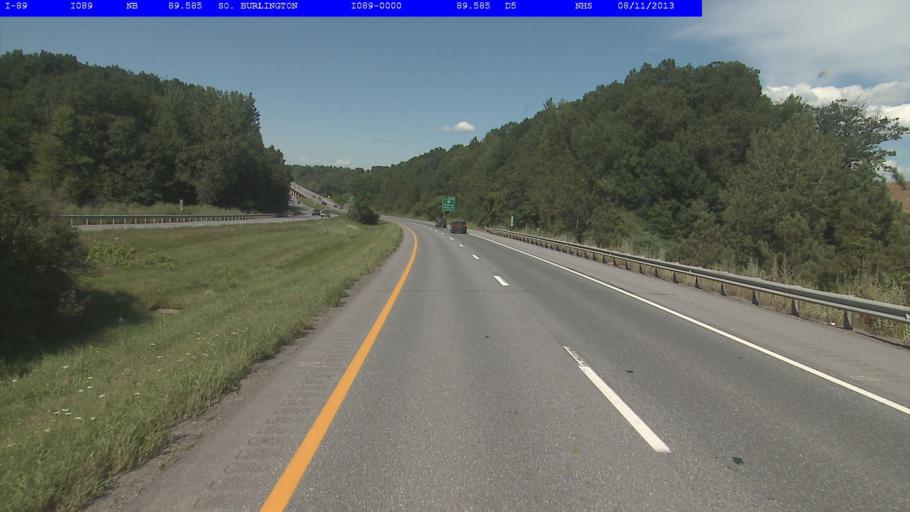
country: US
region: Vermont
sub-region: Chittenden County
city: South Burlington
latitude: 44.4806
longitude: -73.1751
